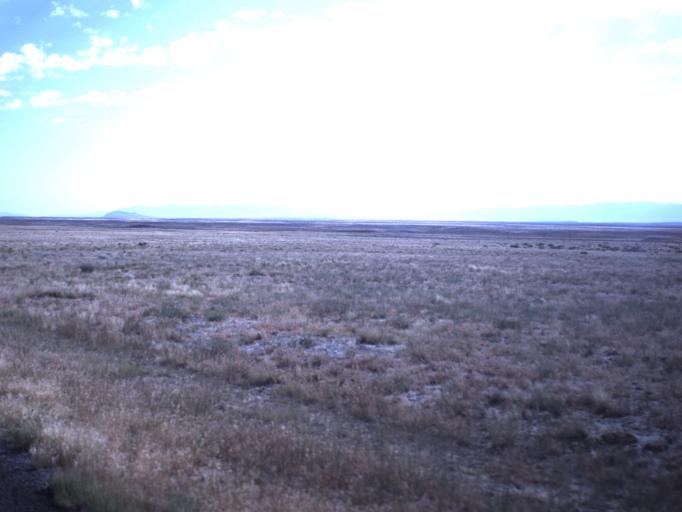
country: US
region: Utah
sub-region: Beaver County
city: Milford
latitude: 38.8505
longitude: -112.8422
